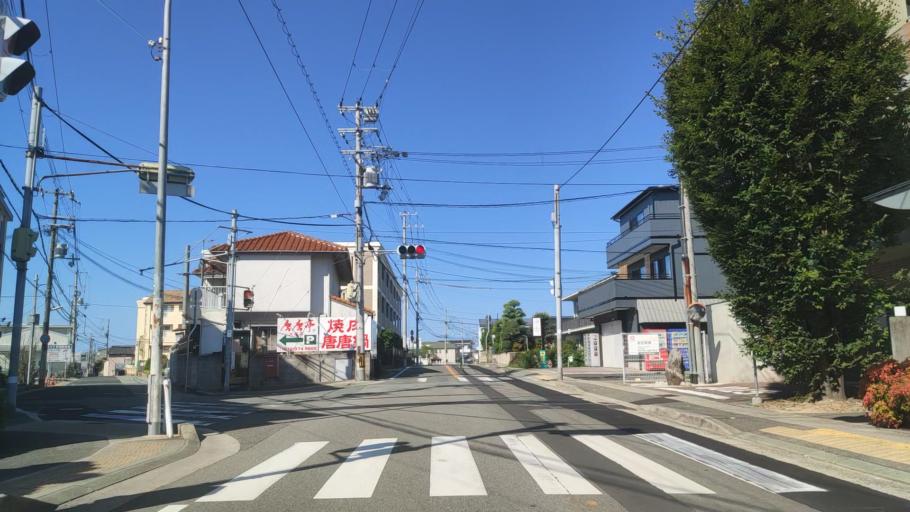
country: JP
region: Hyogo
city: Akashi
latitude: 34.6608
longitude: 135.0212
